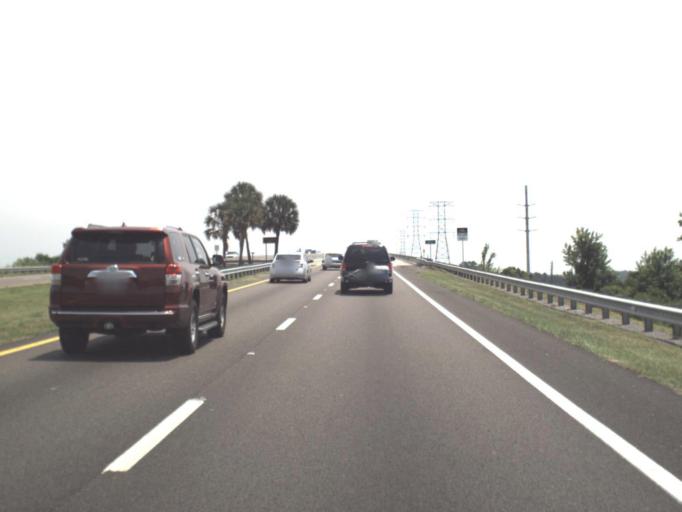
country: US
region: Florida
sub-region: Nassau County
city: Fernandina Beach
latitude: 30.6252
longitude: -81.4895
